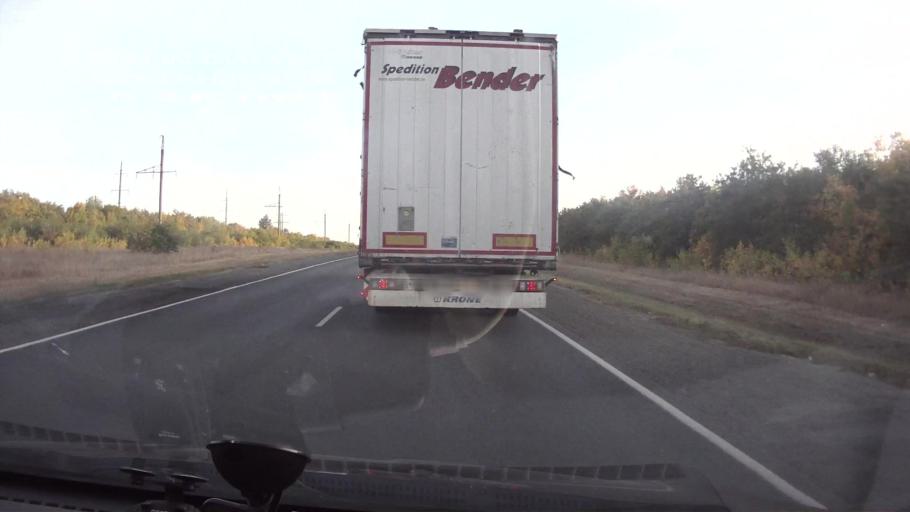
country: RU
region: Saratov
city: Krasnoarmeysk
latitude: 51.1535
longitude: 45.6494
